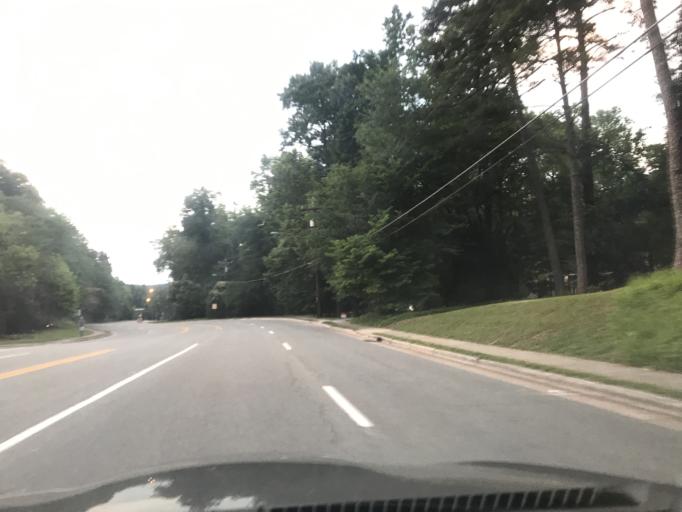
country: US
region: North Carolina
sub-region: Orange County
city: Chapel Hill
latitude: 35.9207
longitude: -79.0388
